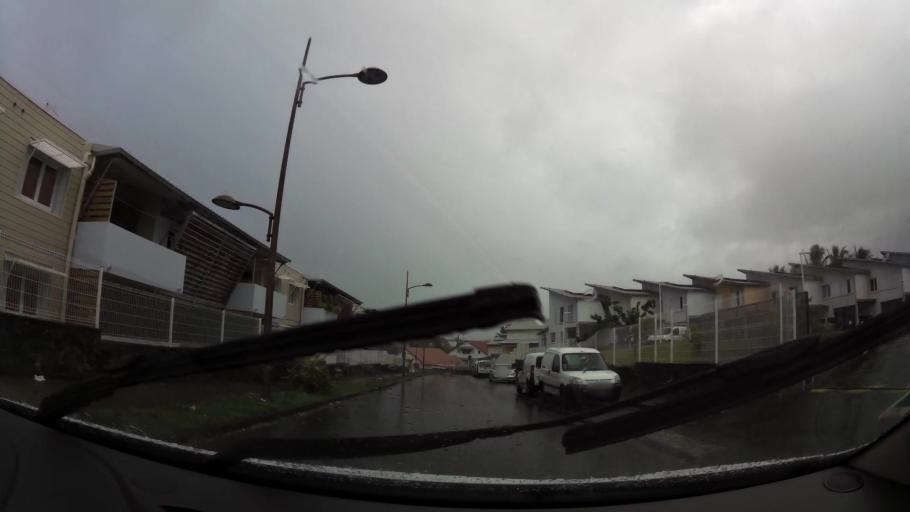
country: RE
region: Reunion
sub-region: Reunion
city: Saint-Benoit
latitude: -21.0302
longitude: 55.6911
